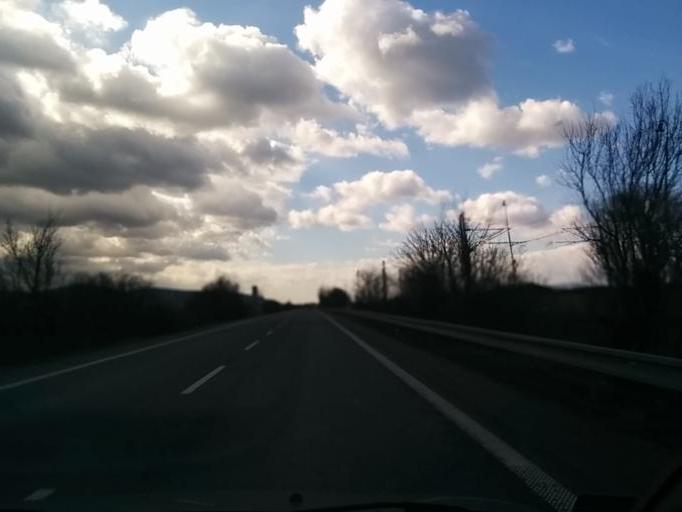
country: SK
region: Trenciansky
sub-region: Okres Trencin
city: Trencin
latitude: 48.8554
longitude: 17.9461
